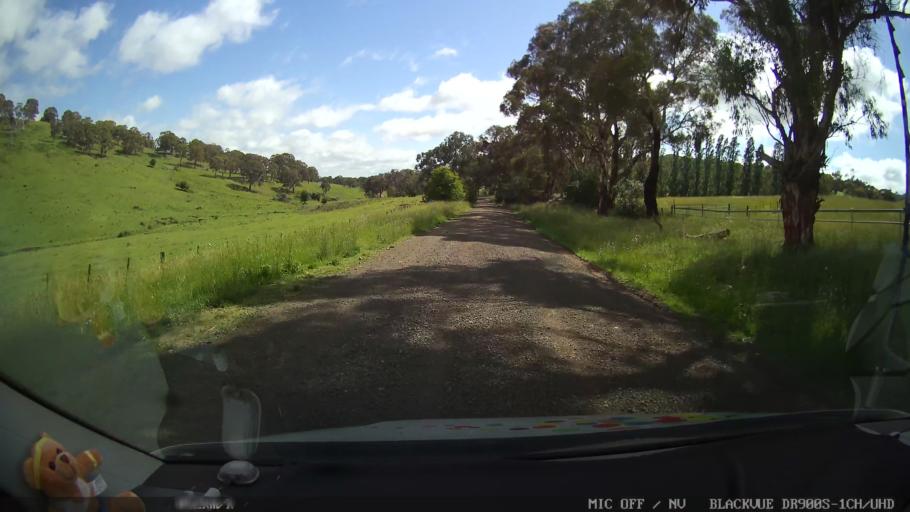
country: AU
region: New South Wales
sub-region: Guyra
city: Guyra
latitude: -29.9862
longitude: 151.6927
